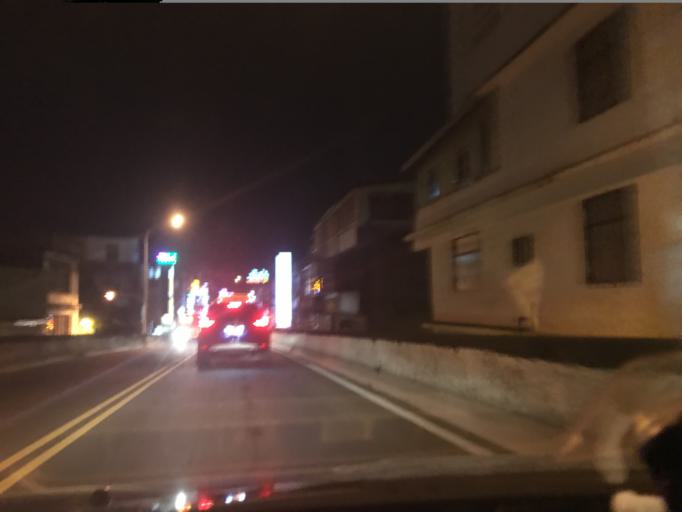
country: TW
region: Taiwan
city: Taoyuan City
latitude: 24.9565
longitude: 121.2346
